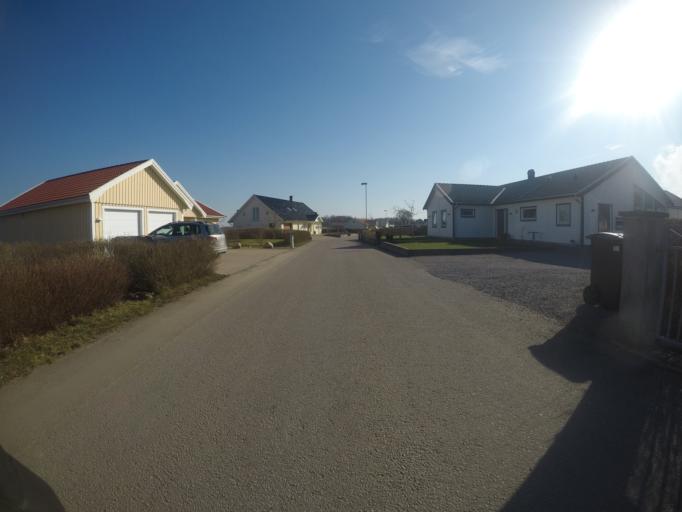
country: SE
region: Halland
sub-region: Laholms Kommun
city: Laholm
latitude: 56.5048
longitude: 13.0664
